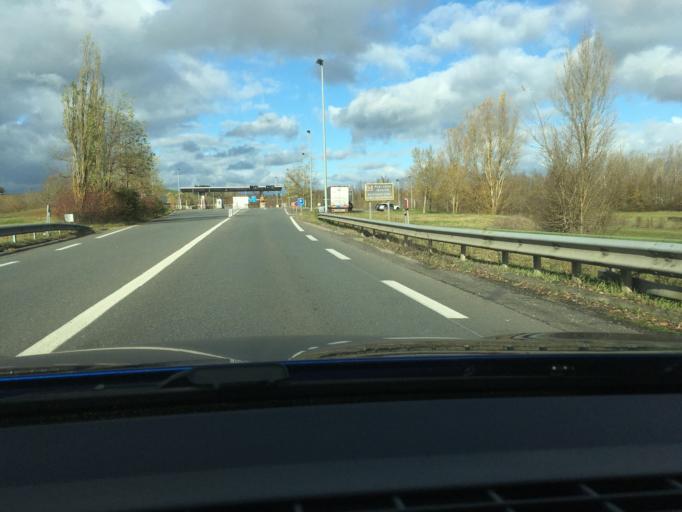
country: FR
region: Midi-Pyrenees
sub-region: Departement du Tarn-et-Garonne
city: Caussade
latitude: 44.1482
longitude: 1.5159
